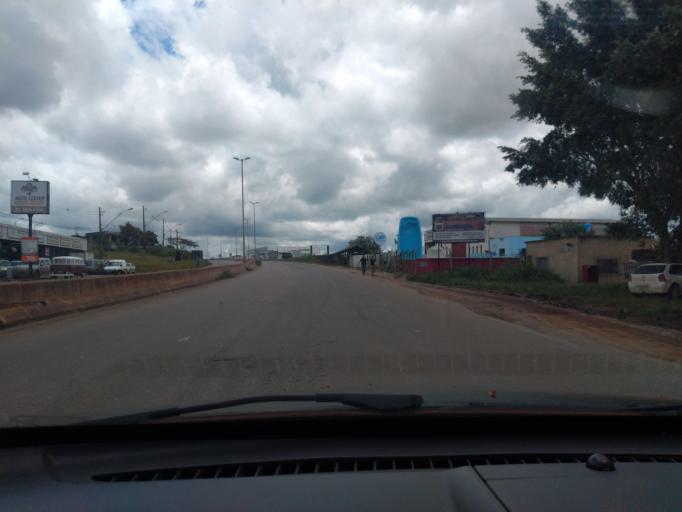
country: BR
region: Minas Gerais
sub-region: Lavras
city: Lavras
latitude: -21.2358
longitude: -45.0285
